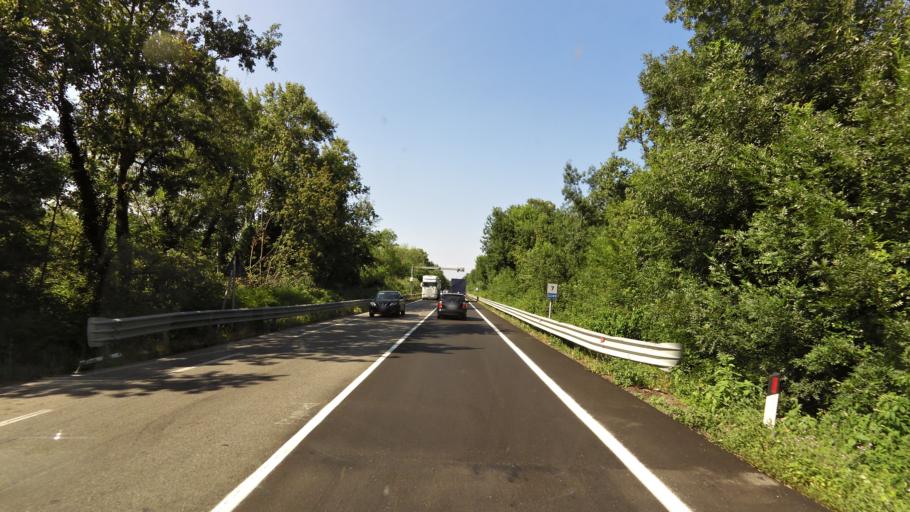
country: IT
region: Emilia-Romagna
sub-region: Provincia di Ravenna
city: Marina Romea
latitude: 44.5170
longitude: 12.2271
